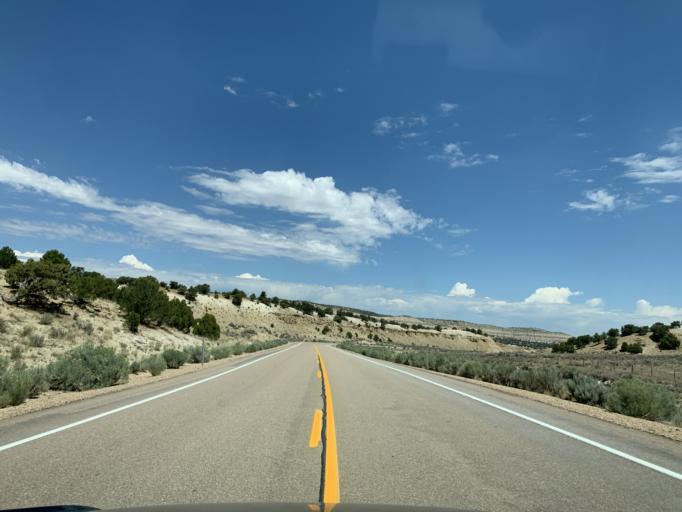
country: US
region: Utah
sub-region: Duchesne County
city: Duchesne
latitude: 39.9206
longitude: -110.2264
